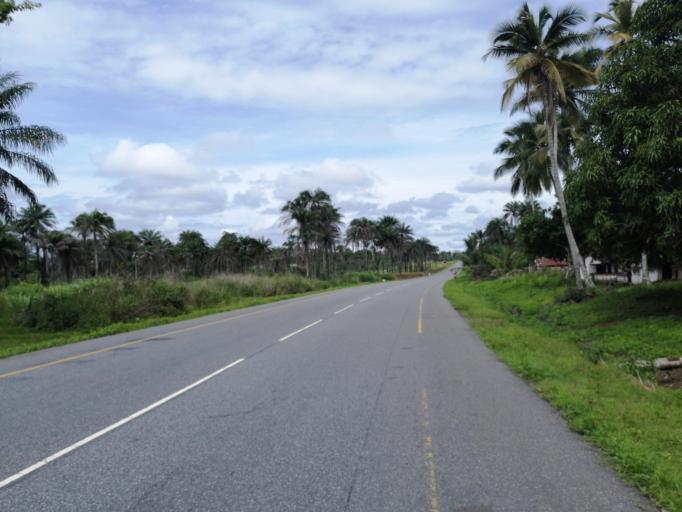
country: SL
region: Northern Province
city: Port Loko
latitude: 8.7278
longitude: -12.9518
